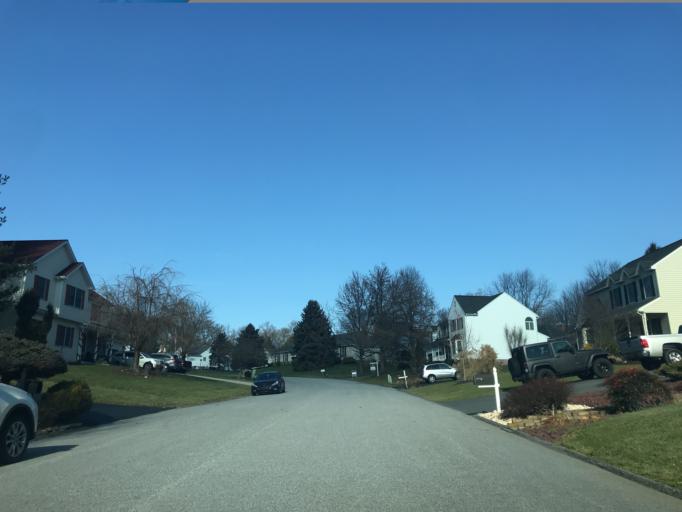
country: US
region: Pennsylvania
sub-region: York County
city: New Freedom
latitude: 39.7324
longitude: -76.6869
